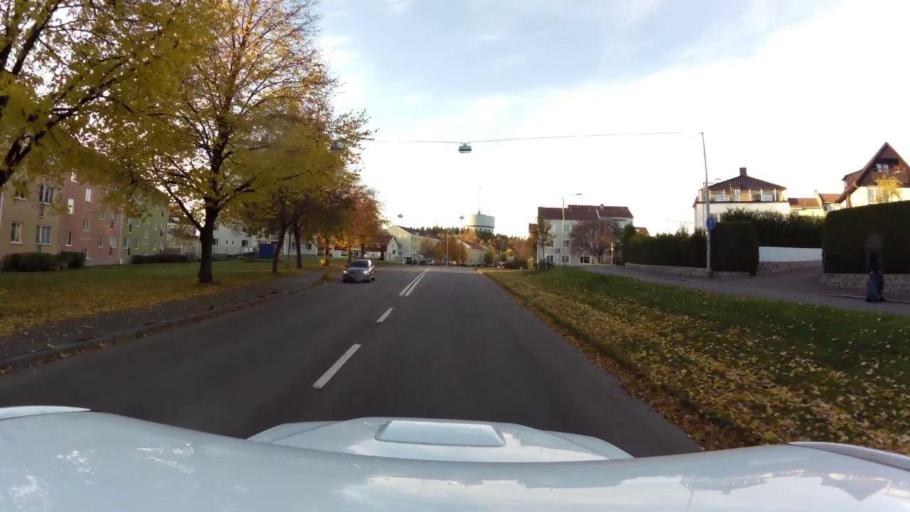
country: SE
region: OEstergoetland
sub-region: Linkopings Kommun
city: Linkoping
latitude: 58.3964
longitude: 15.6408
